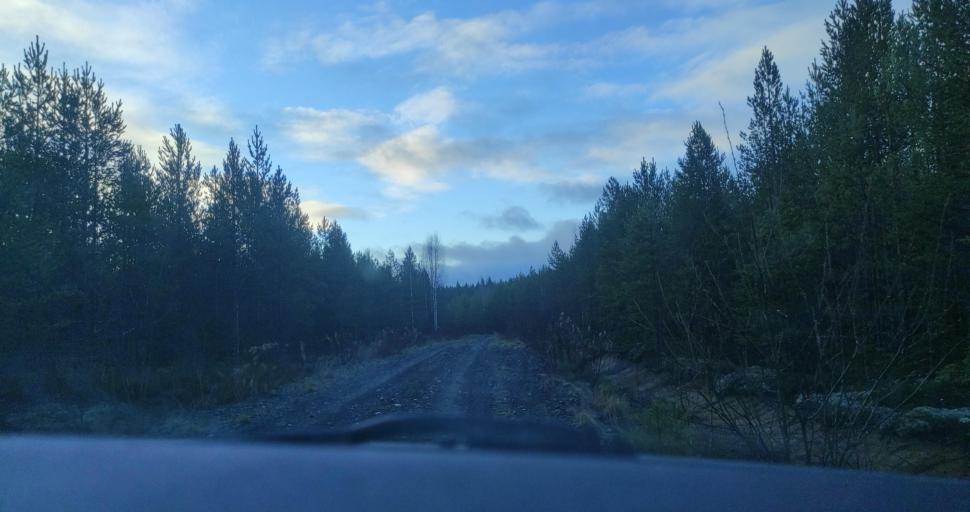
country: RU
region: Republic of Karelia
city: Pitkyaranta
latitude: 61.7386
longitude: 31.3646
